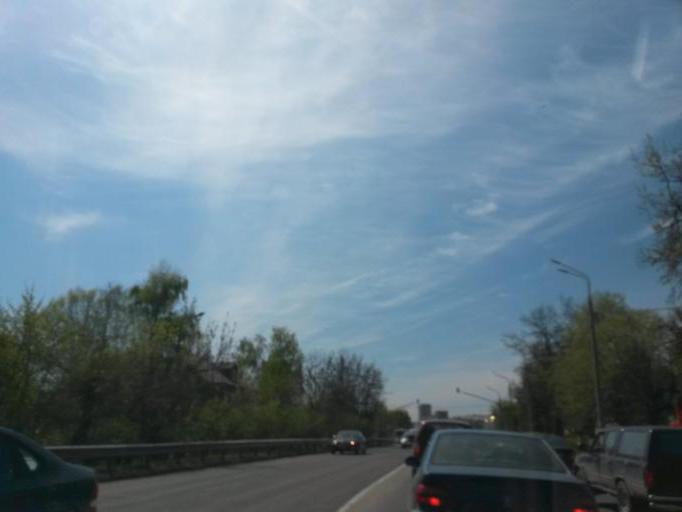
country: RU
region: Moskovskaya
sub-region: Podol'skiy Rayon
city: Podol'sk
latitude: 55.4384
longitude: 37.5563
